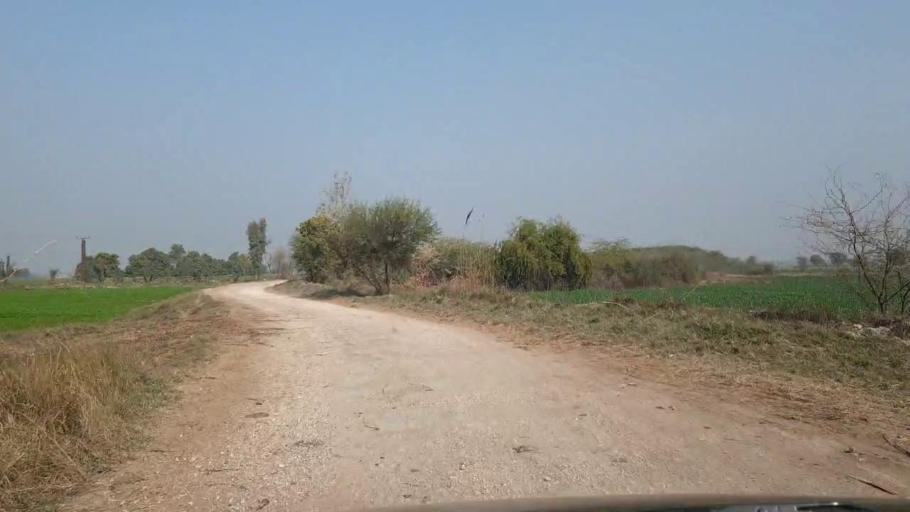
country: PK
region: Sindh
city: Hala
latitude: 25.9709
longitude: 68.4272
